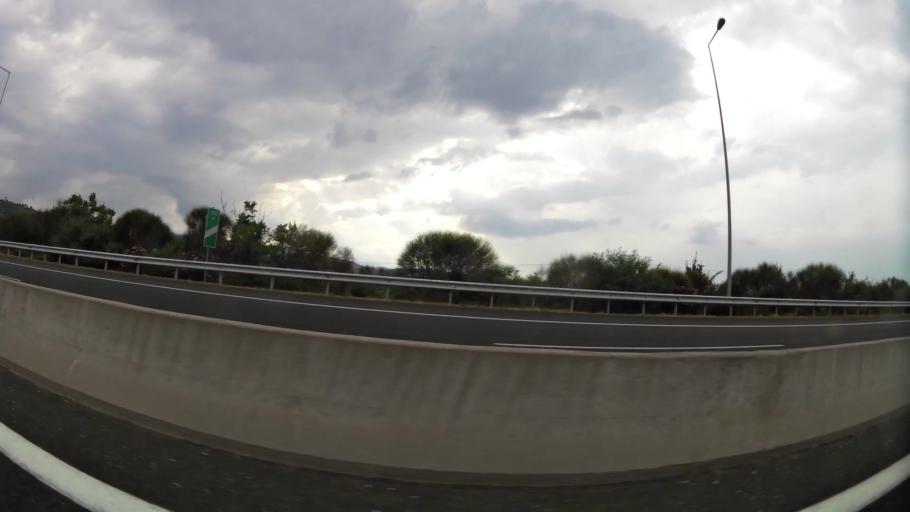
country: GR
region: Central Macedonia
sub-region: Nomos Imathias
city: Veroia
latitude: 40.5107
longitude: 22.2320
